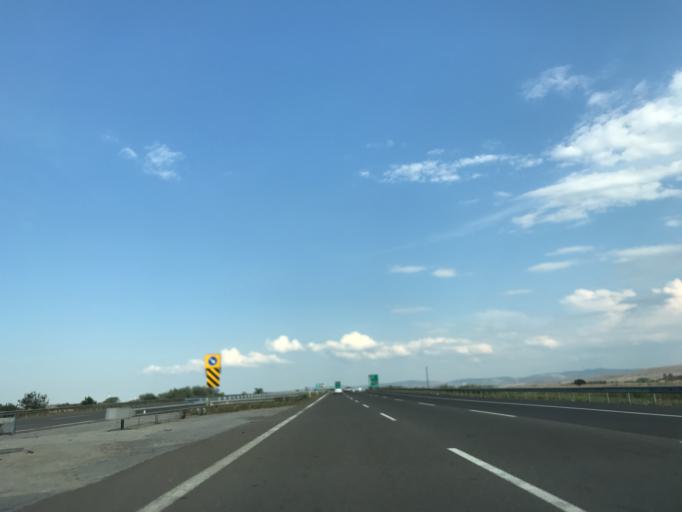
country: TR
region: Bolu
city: Dortdivan
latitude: 40.7463
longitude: 32.1025
